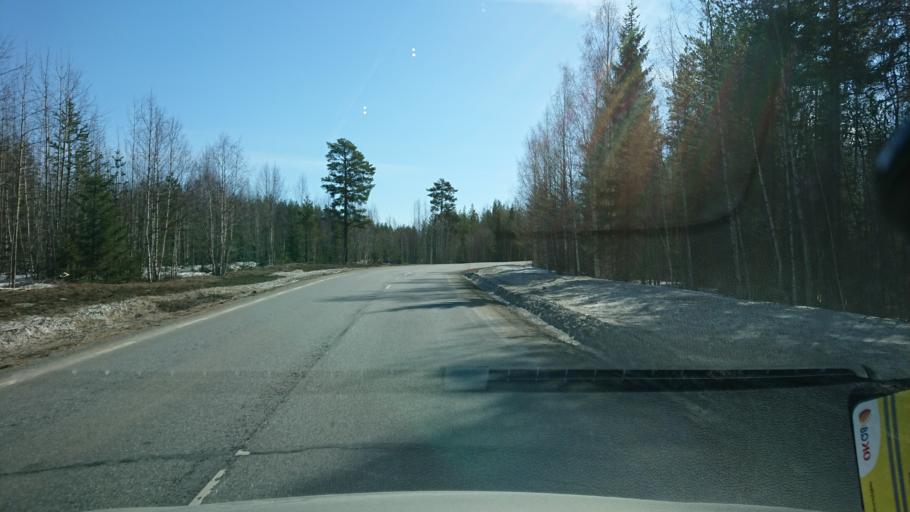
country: SE
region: Vaesterbotten
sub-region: Dorotea Kommun
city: Dorotea
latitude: 64.0074
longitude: 16.3027
